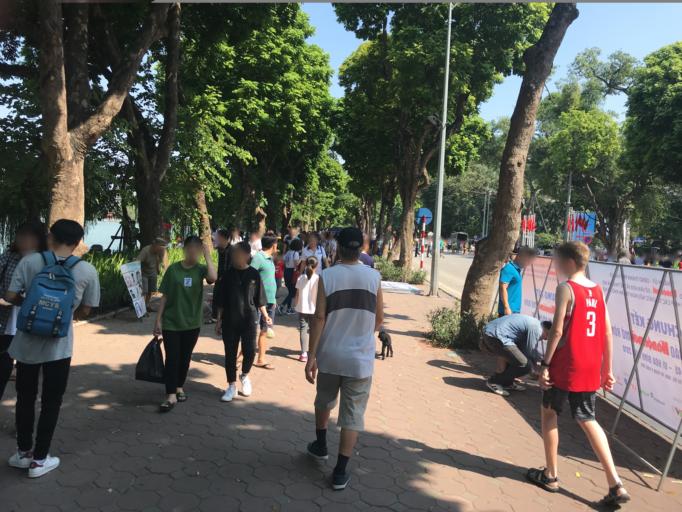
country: VN
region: Ha Noi
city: Hoan Kiem
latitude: 21.0270
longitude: 105.8535
